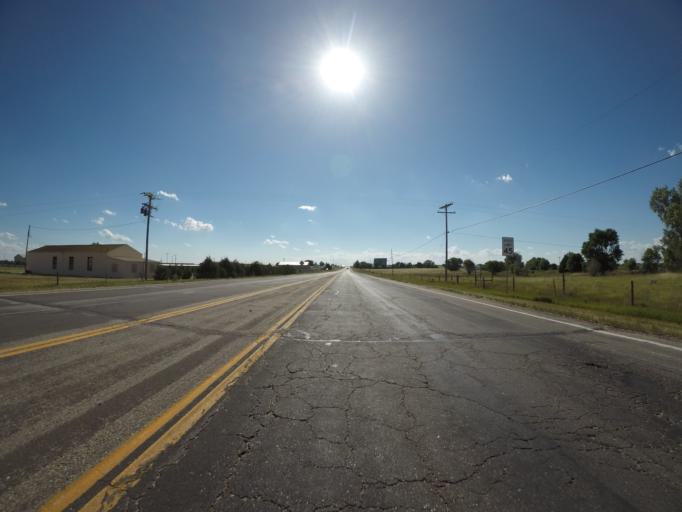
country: US
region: Colorado
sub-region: Logan County
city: Sterling
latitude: 40.6238
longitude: -103.2591
